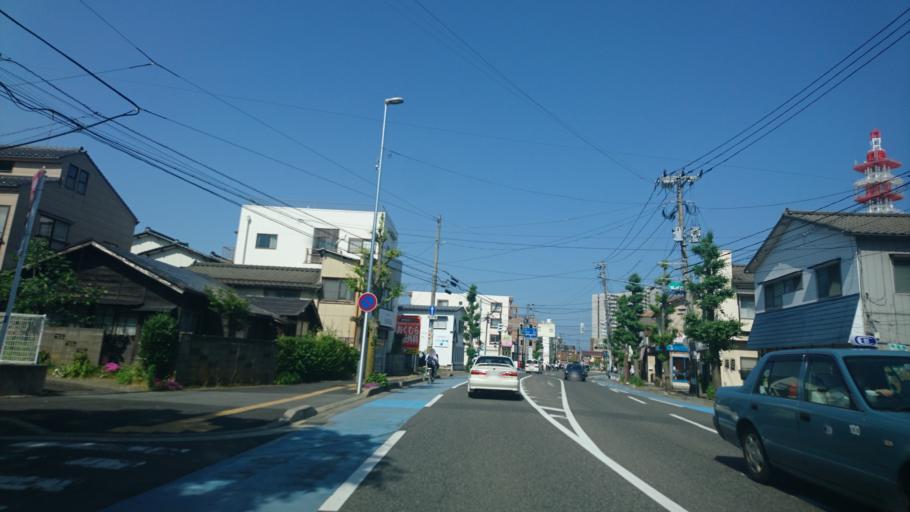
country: JP
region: Niigata
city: Niigata-shi
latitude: 37.9117
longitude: 139.0559
